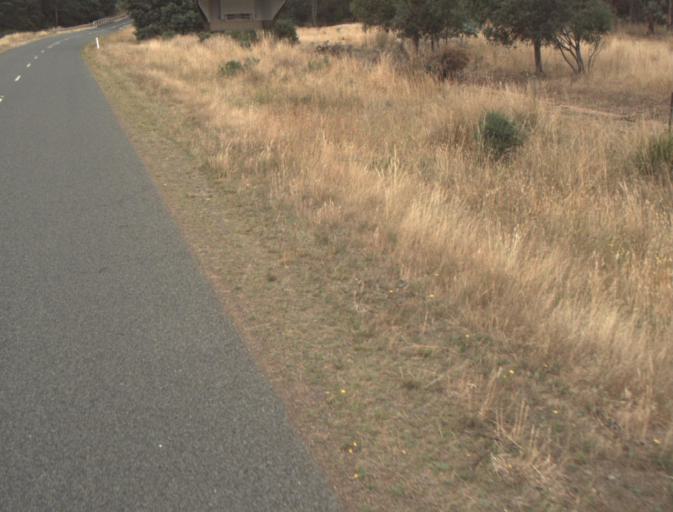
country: AU
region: Tasmania
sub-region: Northern Midlands
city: Evandale
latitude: -41.4878
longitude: 147.5027
